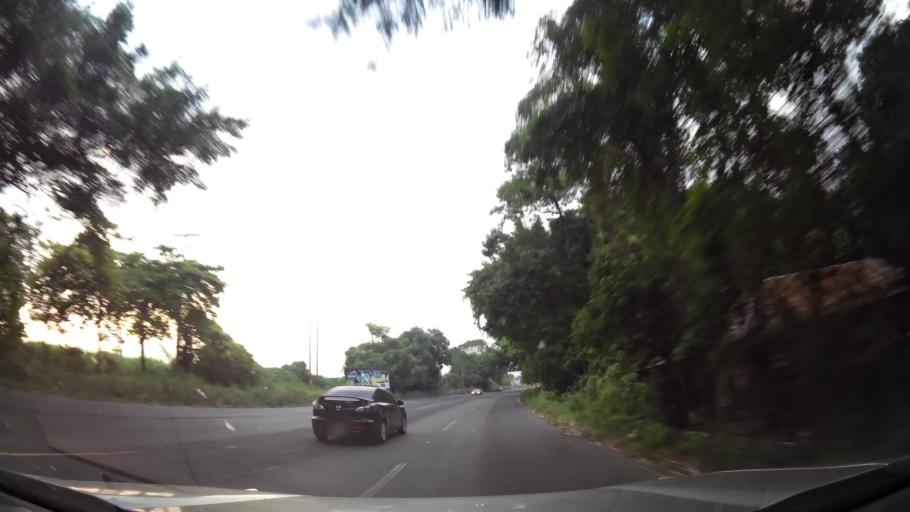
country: GT
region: Escuintla
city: Siquinala
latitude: 14.2840
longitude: -90.9347
